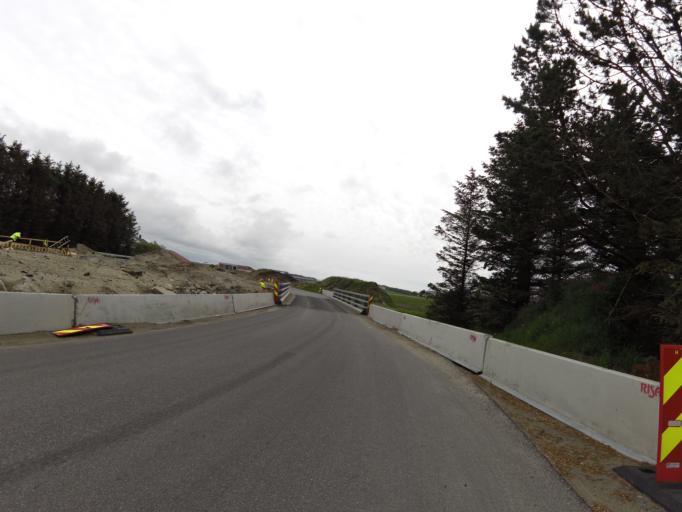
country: NO
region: Rogaland
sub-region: Ha
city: Naerbo
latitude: 58.6872
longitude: 5.5604
